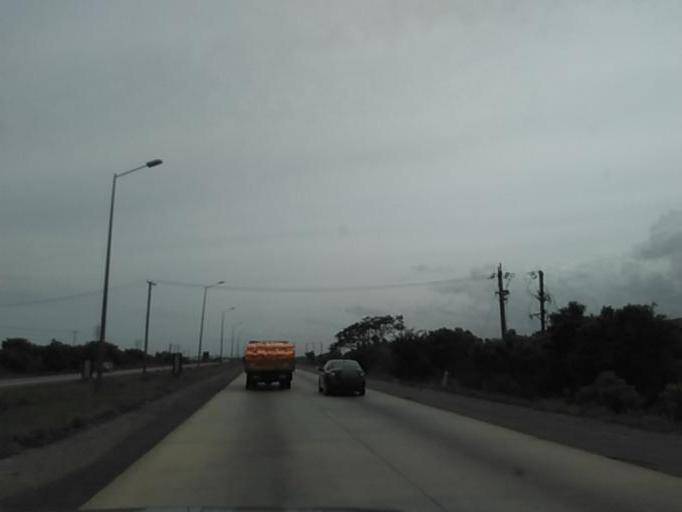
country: GH
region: Greater Accra
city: Nungua
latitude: 5.6550
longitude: -0.0938
